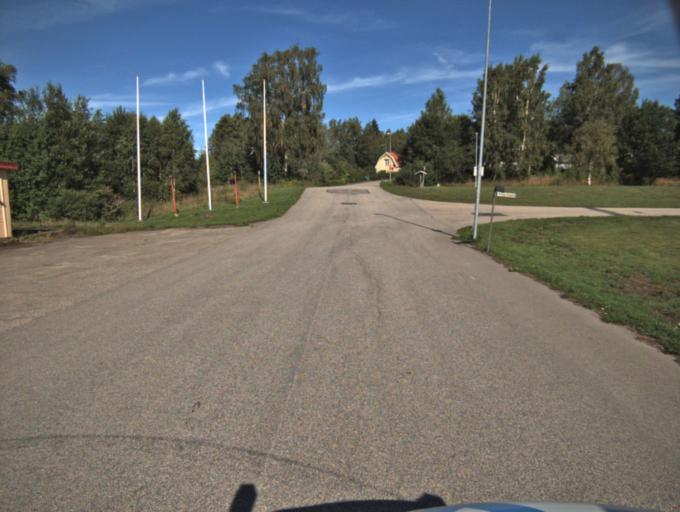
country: SE
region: Vaestra Goetaland
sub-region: Ulricehamns Kommun
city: Ulricehamn
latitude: 57.8997
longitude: 13.4596
